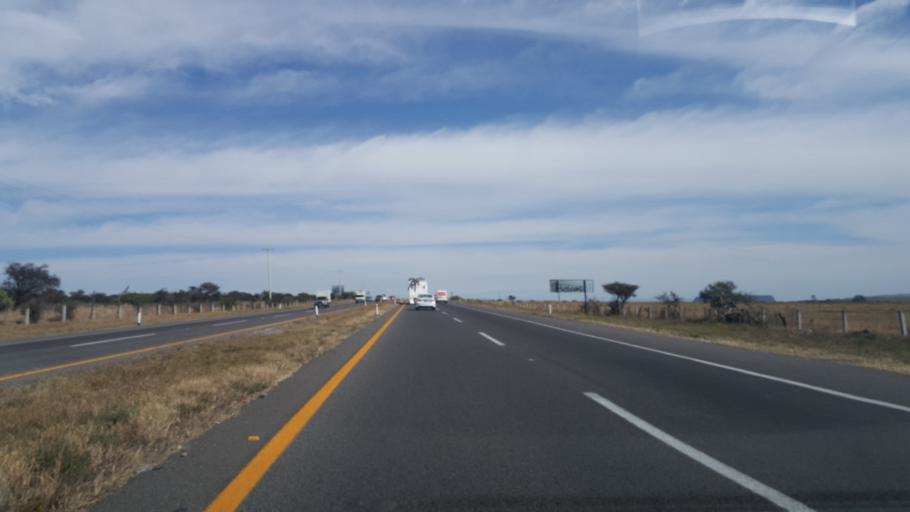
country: MX
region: Jalisco
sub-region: Lagos de Moreno
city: Cristeros [Fraccionamiento]
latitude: 21.3041
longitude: -102.0969
